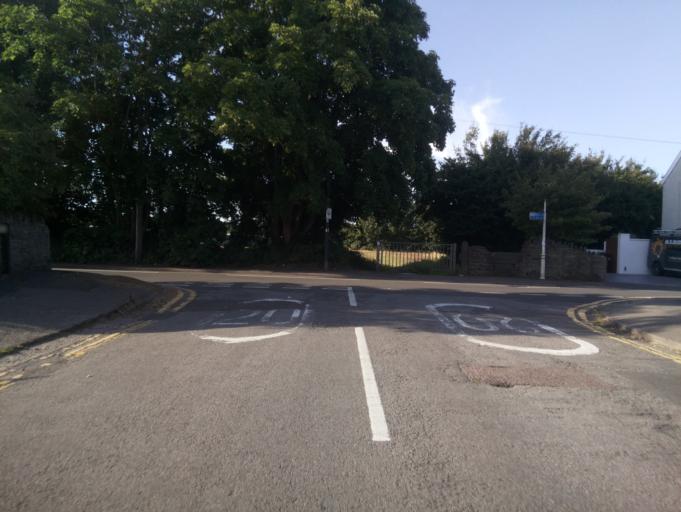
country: GB
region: England
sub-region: South Gloucestershire
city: Mangotsfield
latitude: 51.4837
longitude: -2.4826
